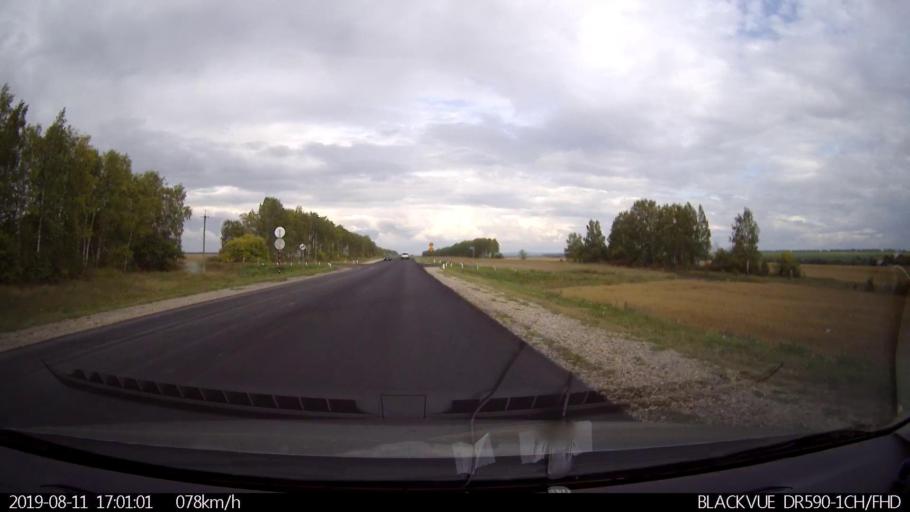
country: RU
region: Ulyanovsk
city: Mayna
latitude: 54.3091
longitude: 47.6900
